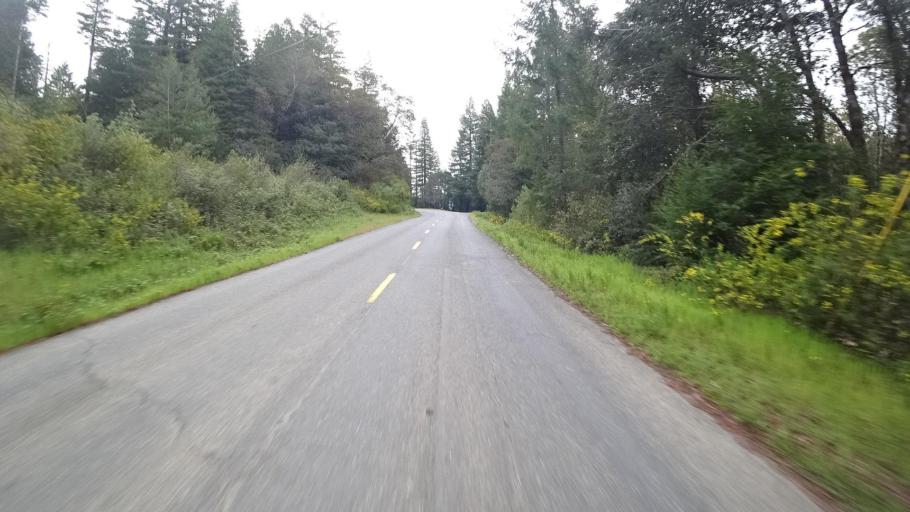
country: US
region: California
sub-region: Humboldt County
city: Redway
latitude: 40.2852
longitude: -123.8385
